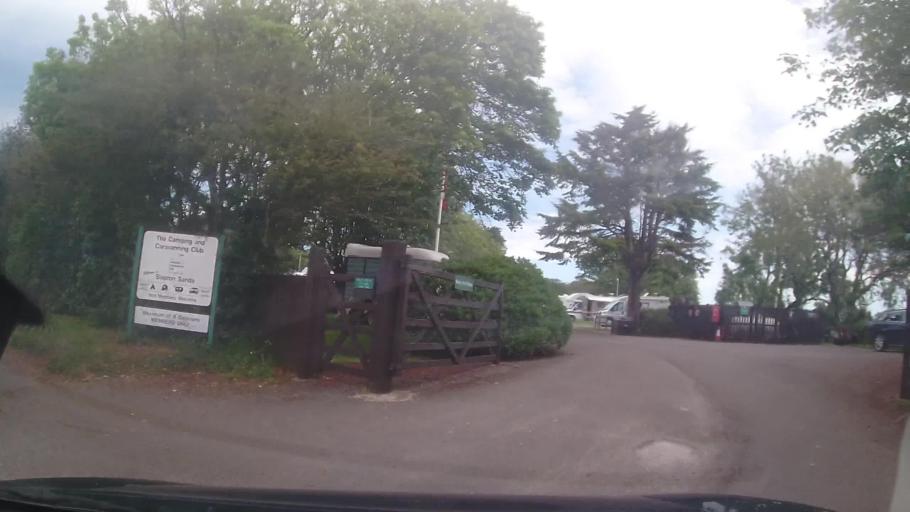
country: GB
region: England
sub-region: Devon
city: Dartmouth
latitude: 50.2906
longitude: -3.6508
